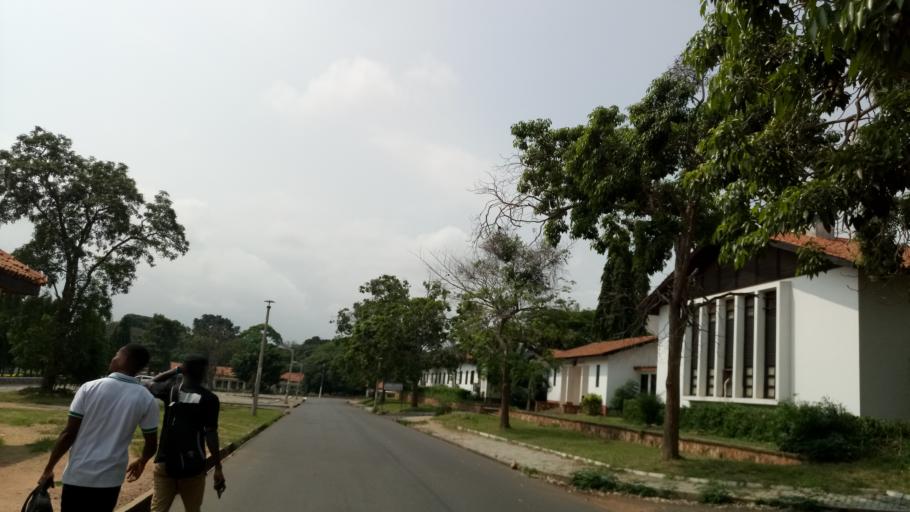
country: GH
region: Greater Accra
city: Medina Estates
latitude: 5.6521
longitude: -0.1862
